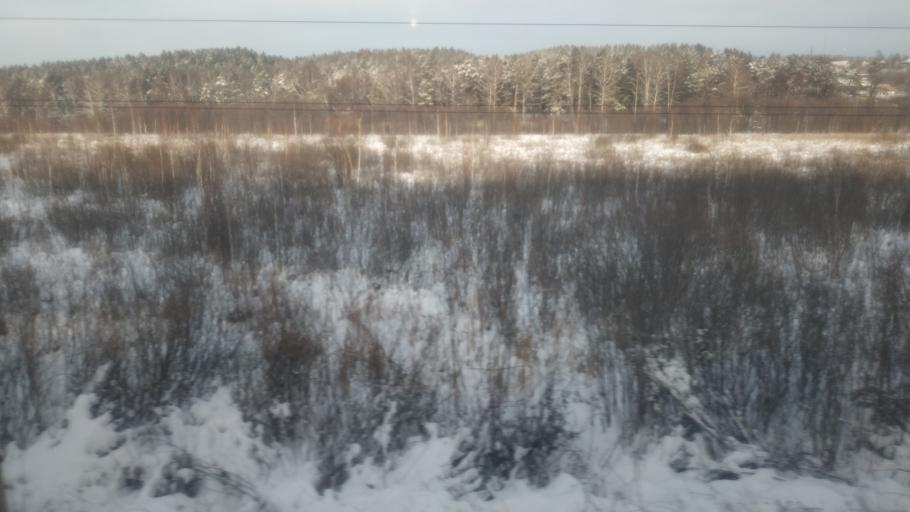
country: RU
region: Kirov
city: Krasnaya Polyana
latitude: 56.2532
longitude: 51.1384
